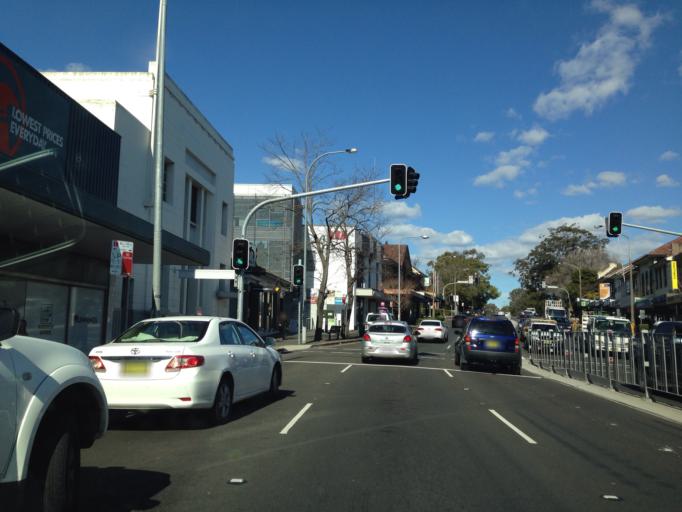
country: AU
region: New South Wales
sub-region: Ku-ring-gai
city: Killara
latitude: -33.7555
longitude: 151.1528
